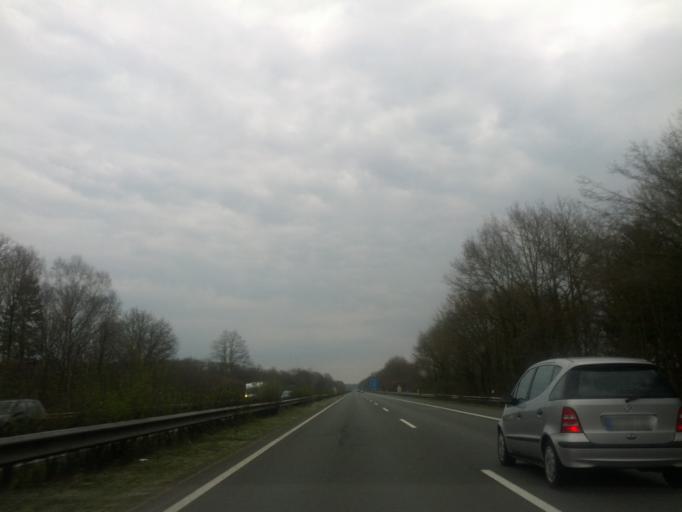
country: DE
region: Lower Saxony
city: Oldenburg
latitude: 53.1601
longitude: 8.1406
